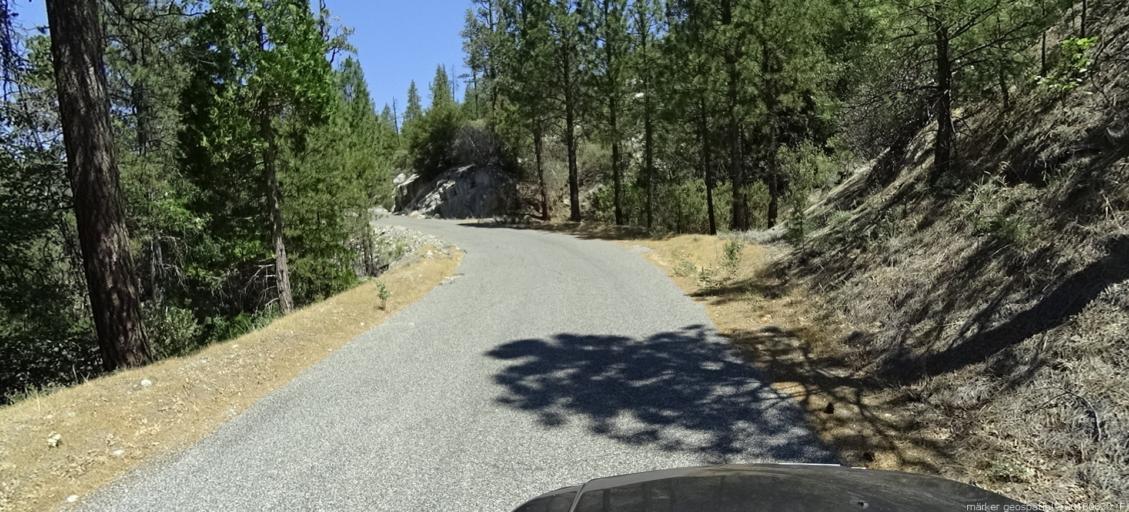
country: US
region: California
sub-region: Madera County
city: Oakhurst
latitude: 37.3691
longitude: -119.3529
